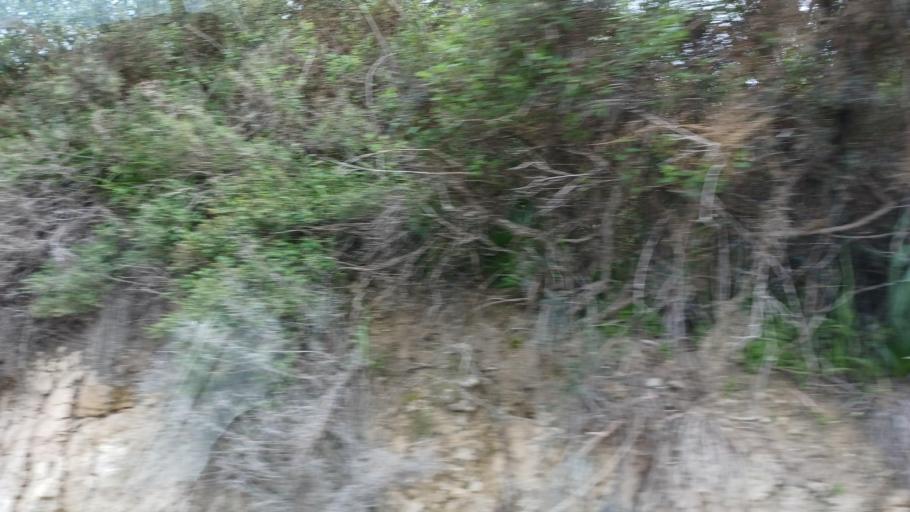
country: CY
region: Pafos
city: Polis
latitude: 35.0474
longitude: 32.4814
